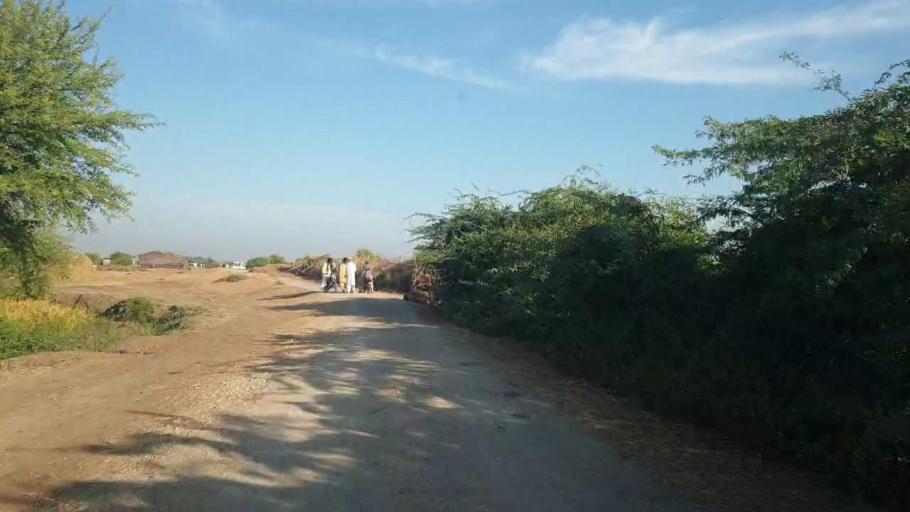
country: PK
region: Sindh
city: Talhar
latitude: 24.8265
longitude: 68.8407
